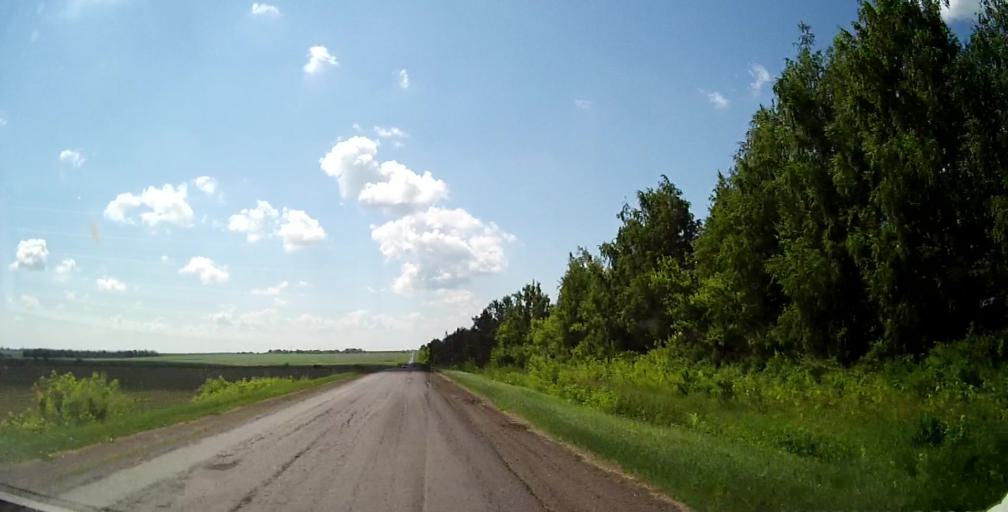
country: RU
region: Lipetsk
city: Chaplygin
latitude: 53.2860
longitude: 39.9589
